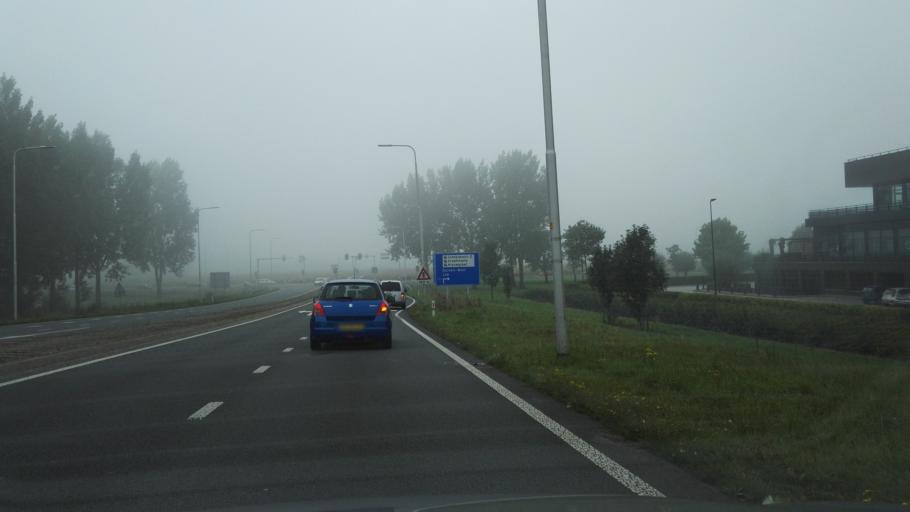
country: NL
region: Gelderland
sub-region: Gemeente Duiven
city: Duiven
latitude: 51.9594
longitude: 6.0230
